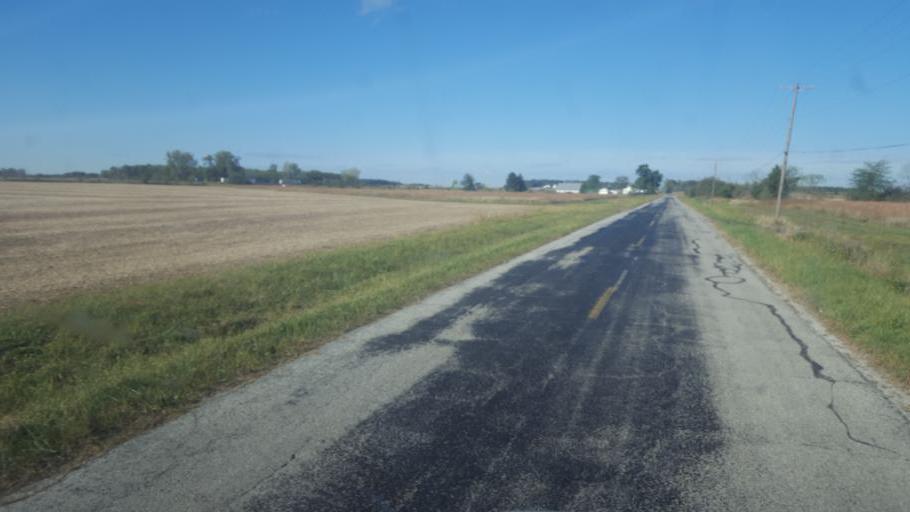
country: US
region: Ohio
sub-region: Marion County
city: Marion
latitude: 40.6882
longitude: -83.1305
